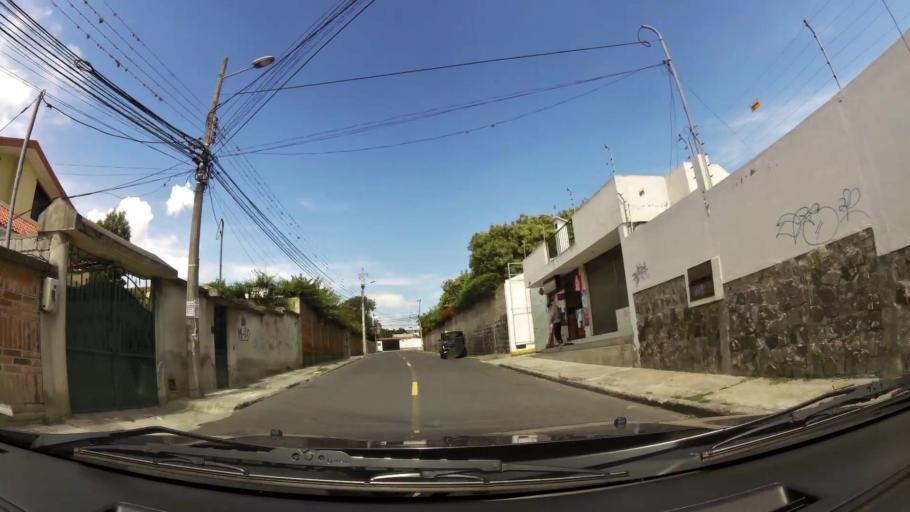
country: EC
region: Pichincha
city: Quito
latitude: -0.2148
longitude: -78.4298
